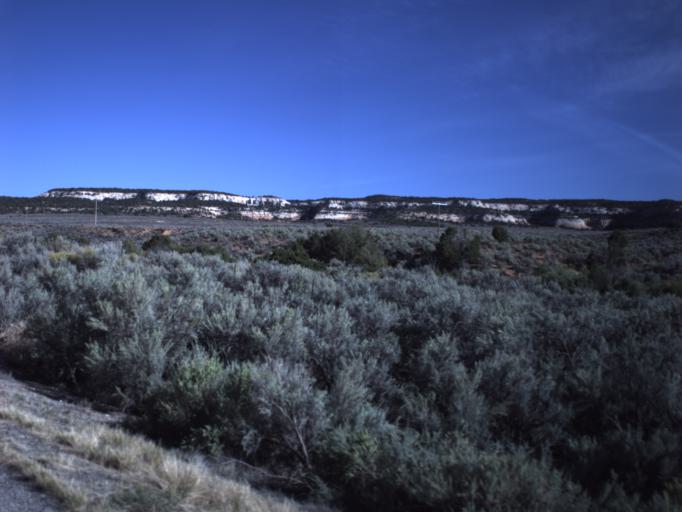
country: US
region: Utah
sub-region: Grand County
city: Moab
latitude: 38.3037
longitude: -109.3797
